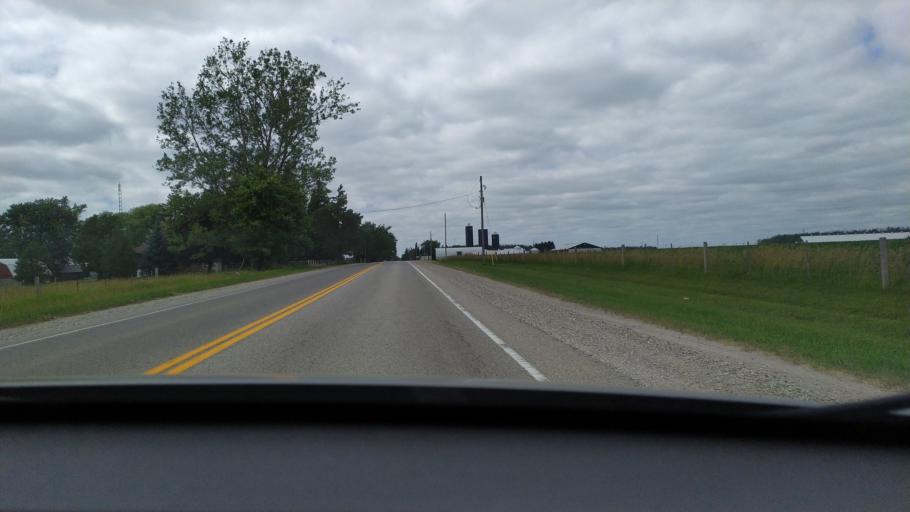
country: CA
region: Ontario
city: Stratford
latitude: 43.3290
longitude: -80.9588
